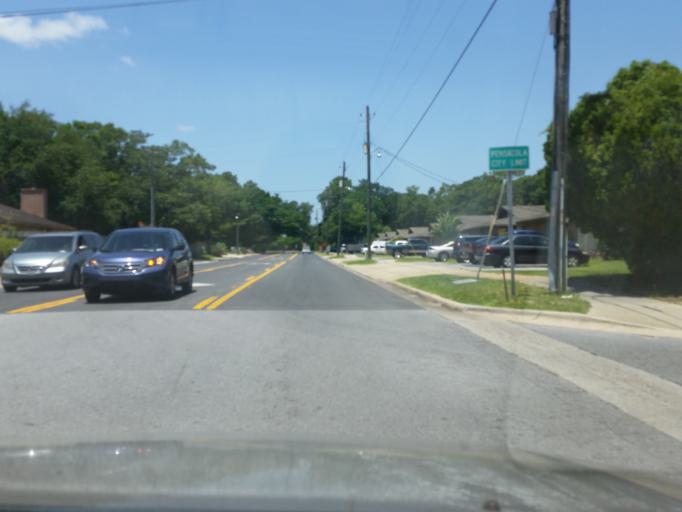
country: US
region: Florida
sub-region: Escambia County
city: Ferry Pass
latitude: 30.4884
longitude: -87.2094
